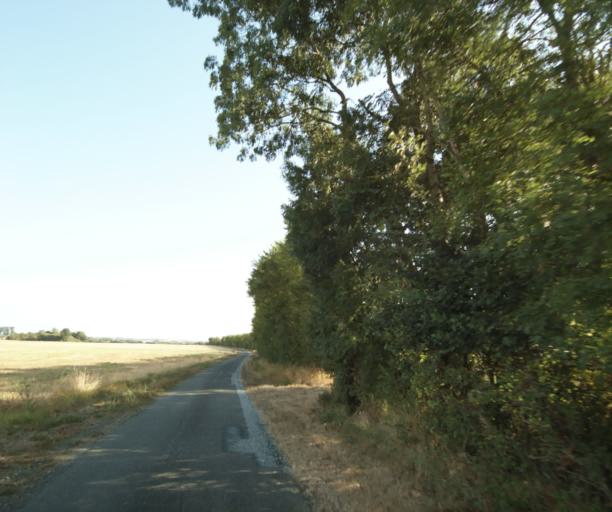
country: FR
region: Poitou-Charentes
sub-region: Departement de la Charente-Maritime
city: Muron
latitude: 45.9773
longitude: -0.8263
